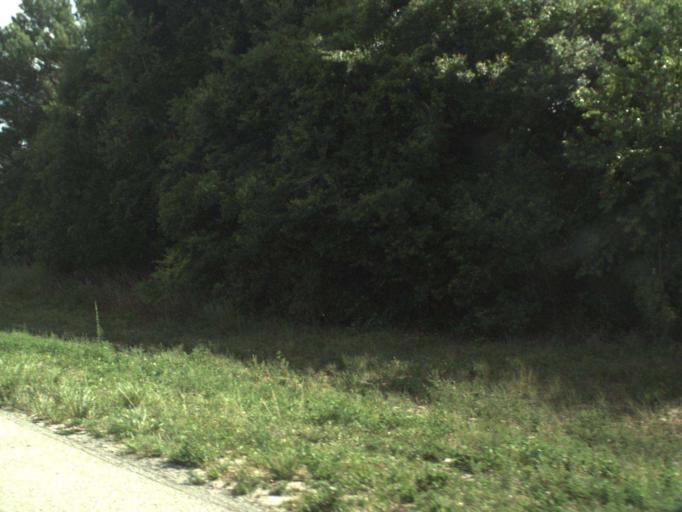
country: US
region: Florida
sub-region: Marion County
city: Silver Springs Shores
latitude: 29.1033
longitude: -82.0536
